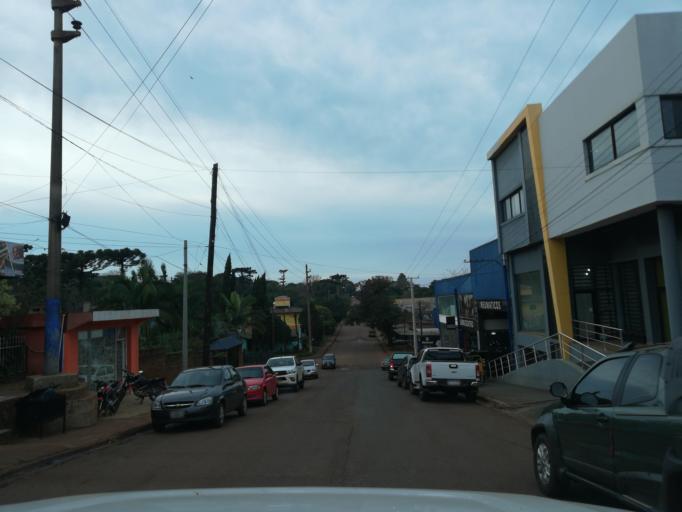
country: AR
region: Misiones
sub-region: Departamento de San Pedro
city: San Pedro
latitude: -26.6210
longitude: -54.1067
